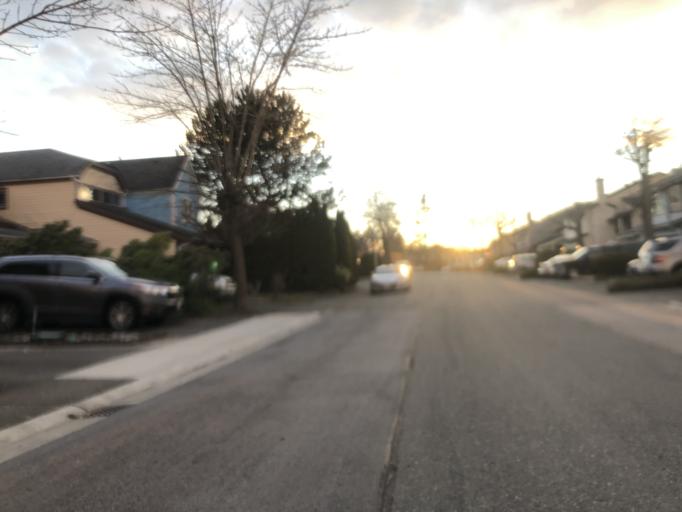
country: CA
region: British Columbia
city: Richmond
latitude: 49.1546
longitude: -123.1179
